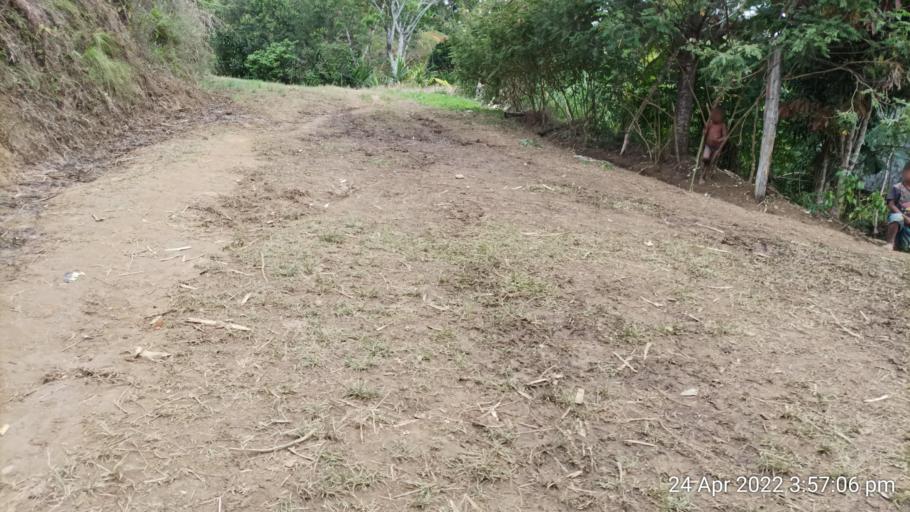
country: PG
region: Jiwaka
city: Minj
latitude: -5.8993
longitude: 144.8235
